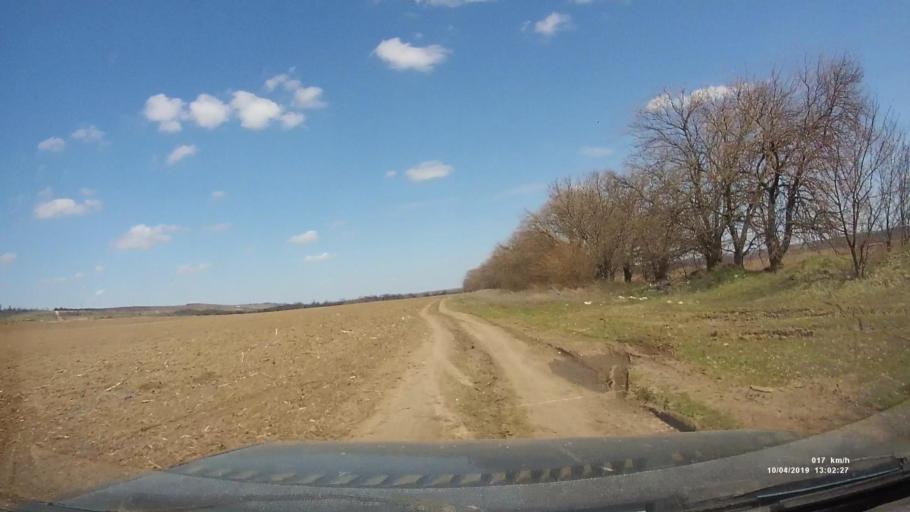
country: RU
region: Rostov
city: Masalovka
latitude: 48.3813
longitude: 40.2309
